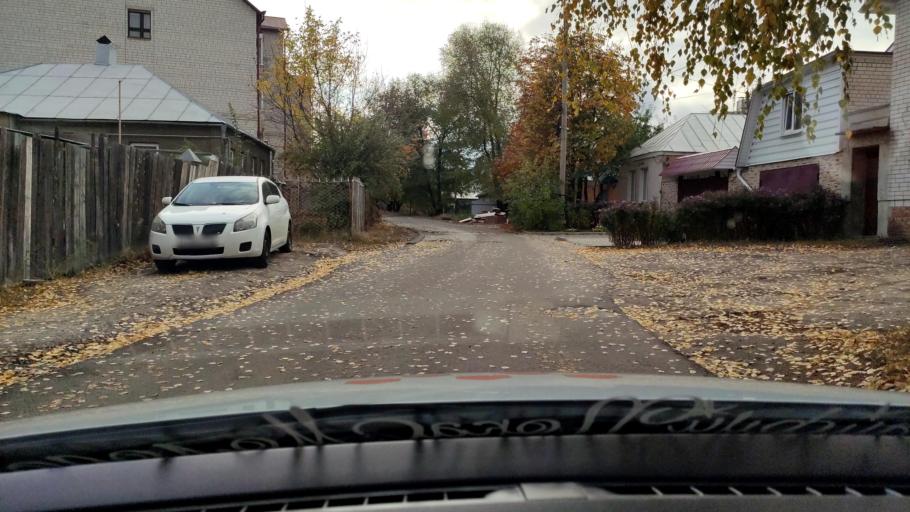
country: RU
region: Voronezj
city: Voronezh
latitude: 51.6900
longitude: 39.2017
